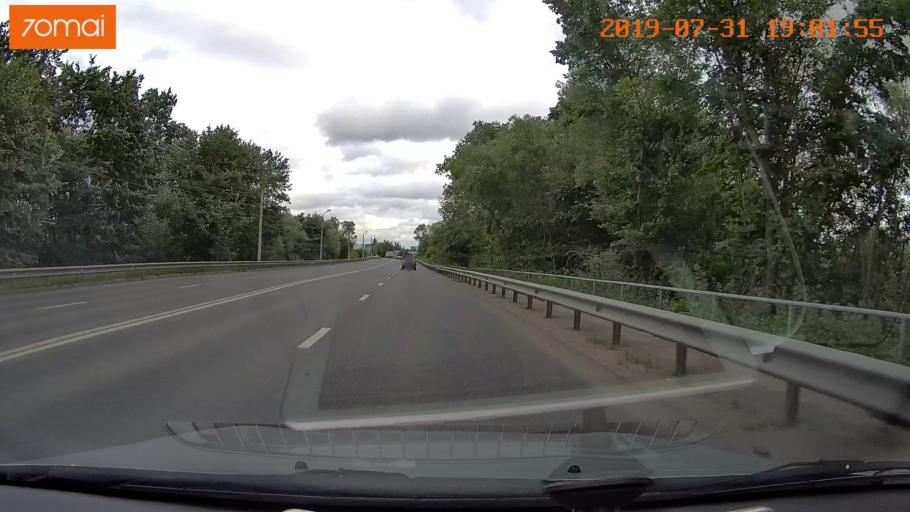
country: RU
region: Moskovskaya
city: Raduzhnyy
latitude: 55.1231
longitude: 38.7298
